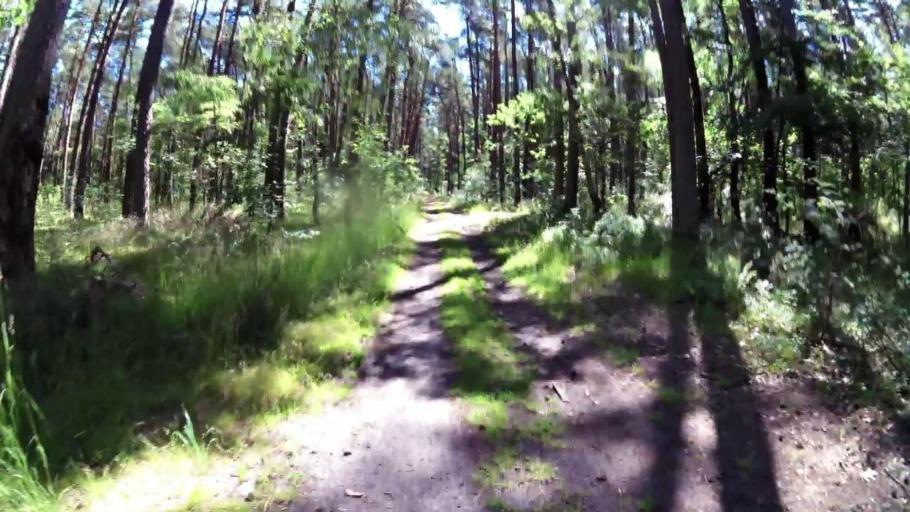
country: PL
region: West Pomeranian Voivodeship
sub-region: Powiat kamienski
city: Dziwnow
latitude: 54.0404
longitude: 14.8395
